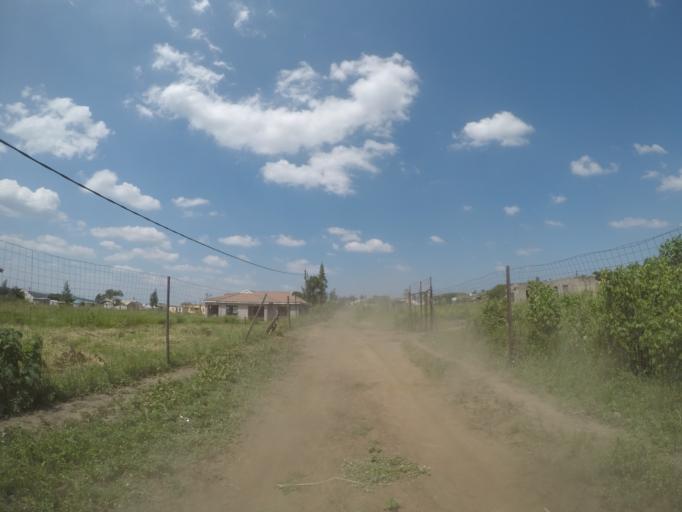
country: ZA
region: KwaZulu-Natal
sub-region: uThungulu District Municipality
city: Empangeni
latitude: -28.5899
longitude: 31.7376
